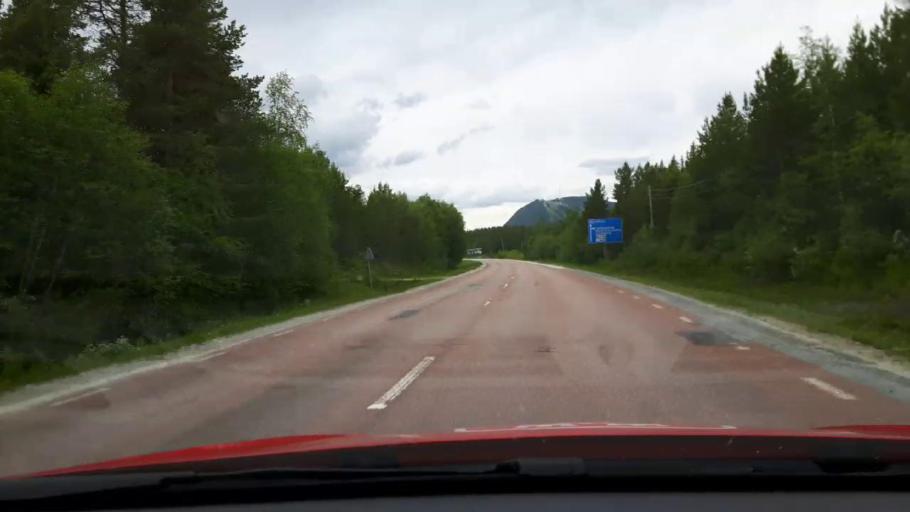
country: NO
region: Hedmark
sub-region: Engerdal
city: Engerdal
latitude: 62.5212
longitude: 12.5930
